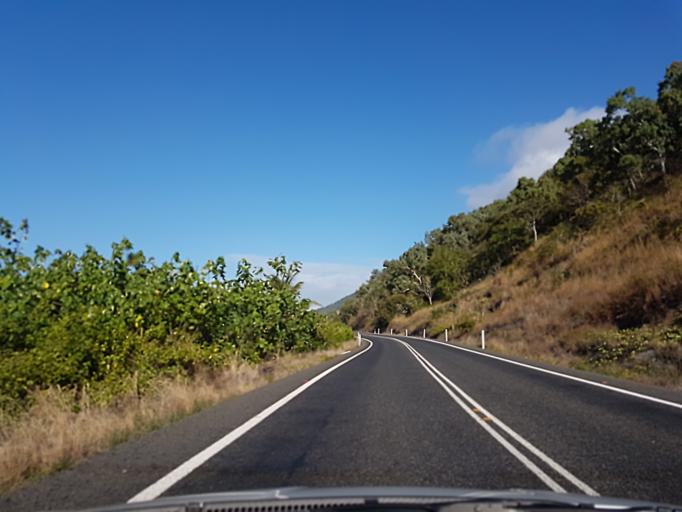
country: AU
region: Queensland
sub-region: Cairns
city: Palm Cove
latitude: -16.7147
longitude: 145.6364
